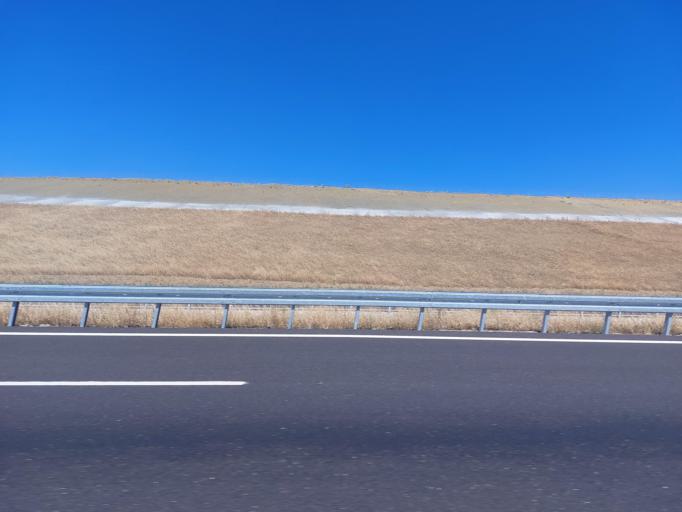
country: TR
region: Canakkale
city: Evrese
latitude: 40.7049
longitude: 26.9792
